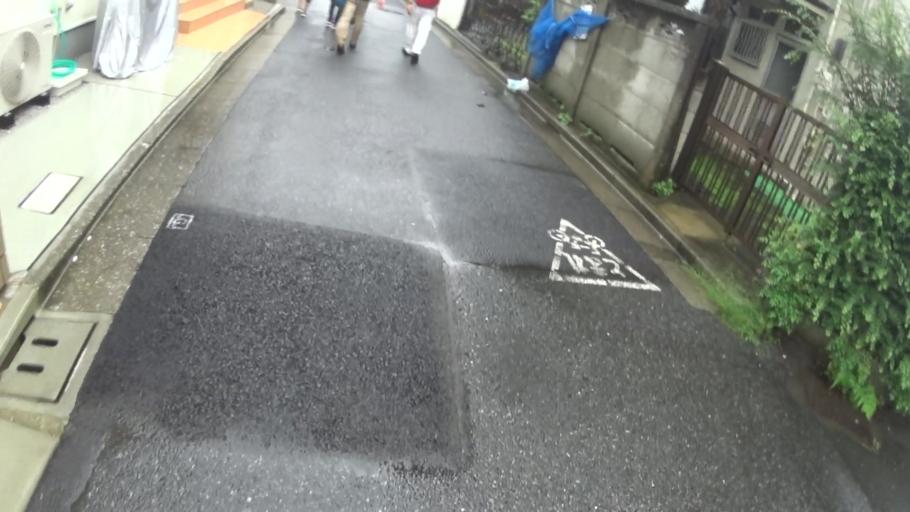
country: JP
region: Saitama
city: Wako
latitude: 35.7453
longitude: 139.6651
